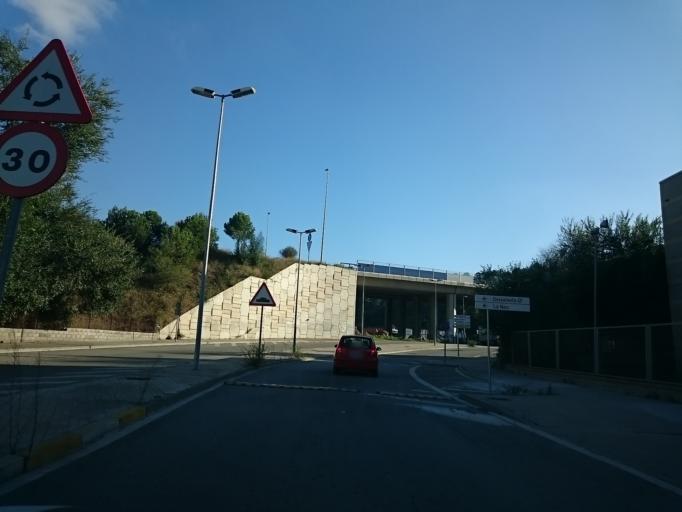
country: ES
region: Catalonia
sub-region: Provincia de Barcelona
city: Palleja
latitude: 41.4159
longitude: 2.0003
